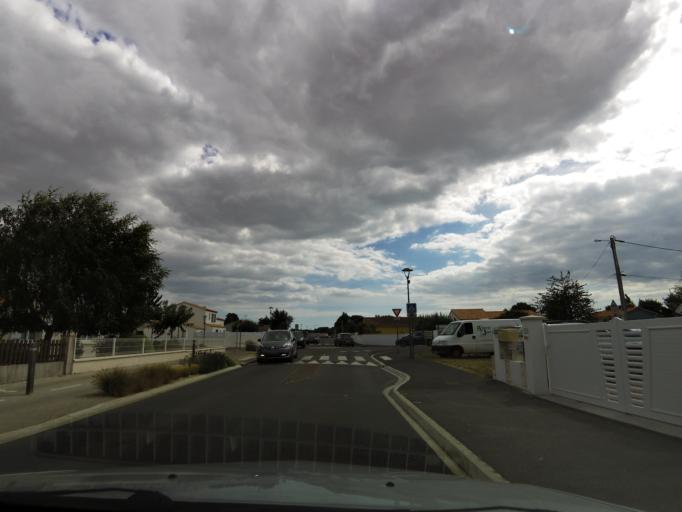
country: FR
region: Pays de la Loire
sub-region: Departement de la Vendee
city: Longeville-sur-Mer
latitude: 46.4192
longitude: -1.4943
